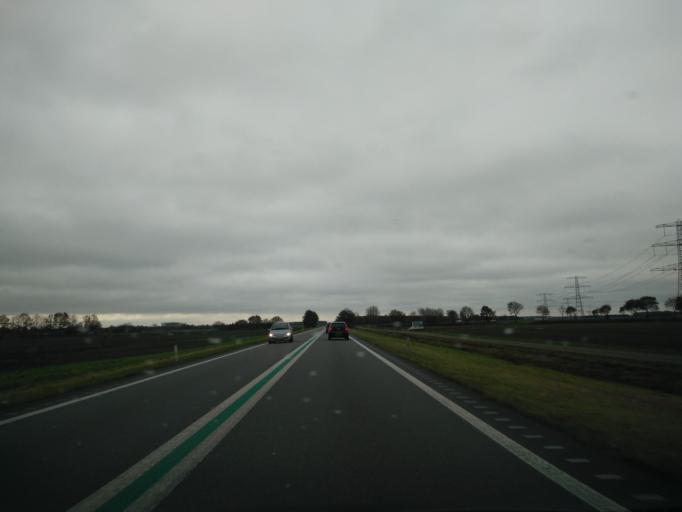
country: NL
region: Drenthe
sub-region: Gemeente Emmen
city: Emmer-Compascuum
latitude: 52.9125
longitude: 7.0377
